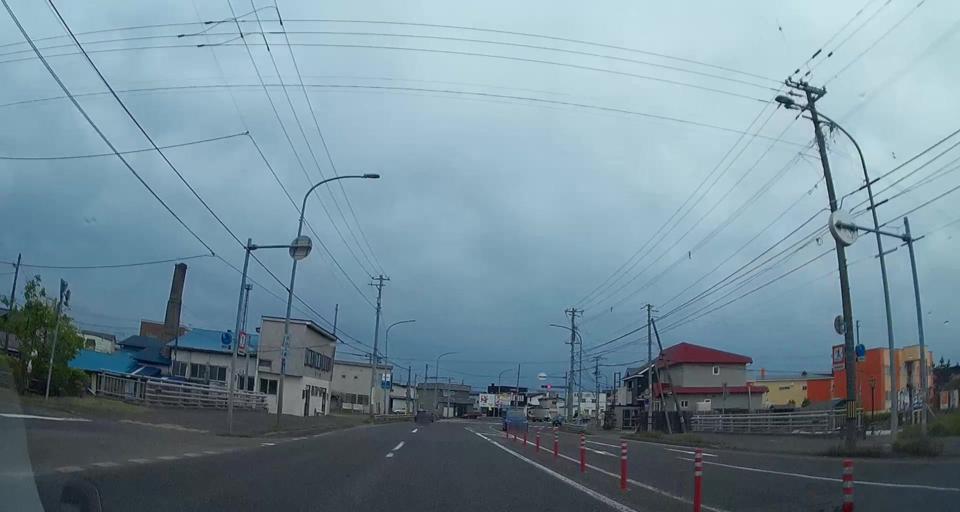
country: JP
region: Hokkaido
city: Tomakomai
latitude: 42.6276
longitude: 141.5934
